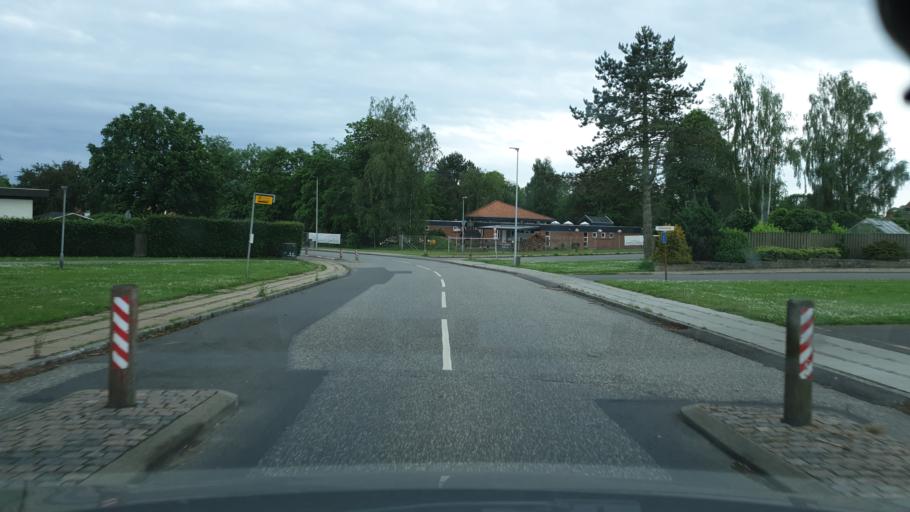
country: DK
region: South Denmark
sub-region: Kolding Kommune
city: Kolding
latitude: 55.5029
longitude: 9.4967
